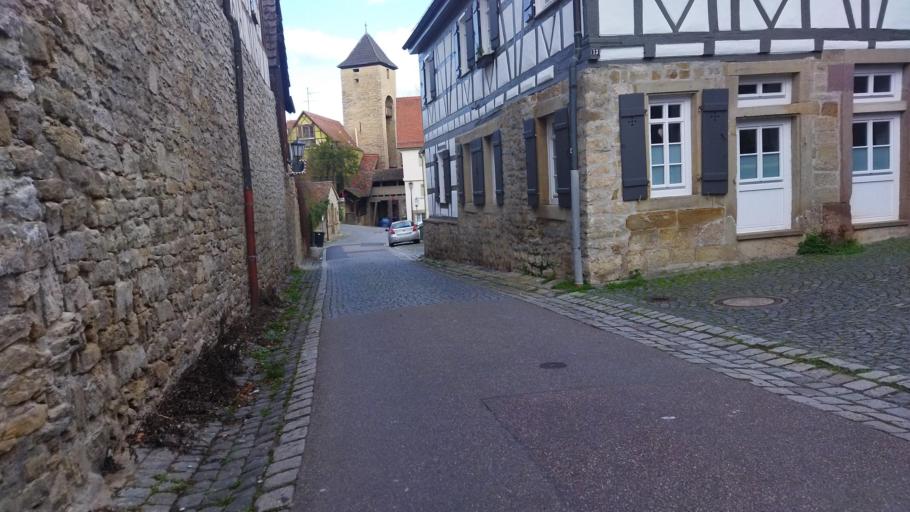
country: DE
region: Baden-Wuerttemberg
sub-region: Regierungsbezirk Stuttgart
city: Bietigheim-Bissingen
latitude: 48.9604
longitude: 9.1275
